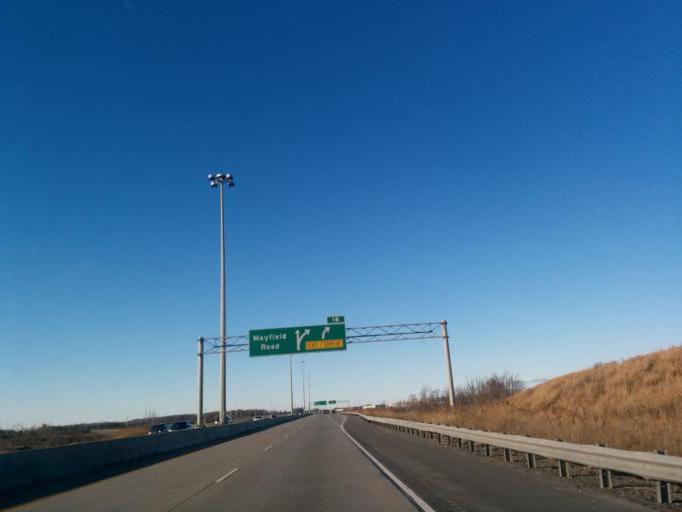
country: CA
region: Ontario
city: Brampton
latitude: 43.7491
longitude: -79.7892
